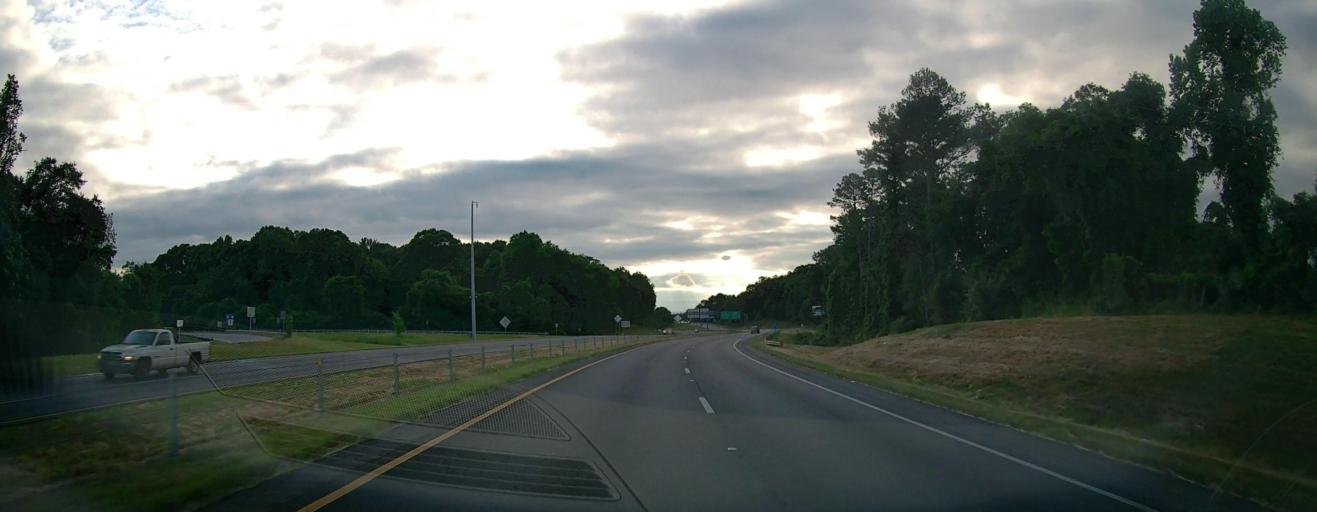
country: US
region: Georgia
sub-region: Clarke County
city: Country Club Estates
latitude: 33.9707
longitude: -83.4046
